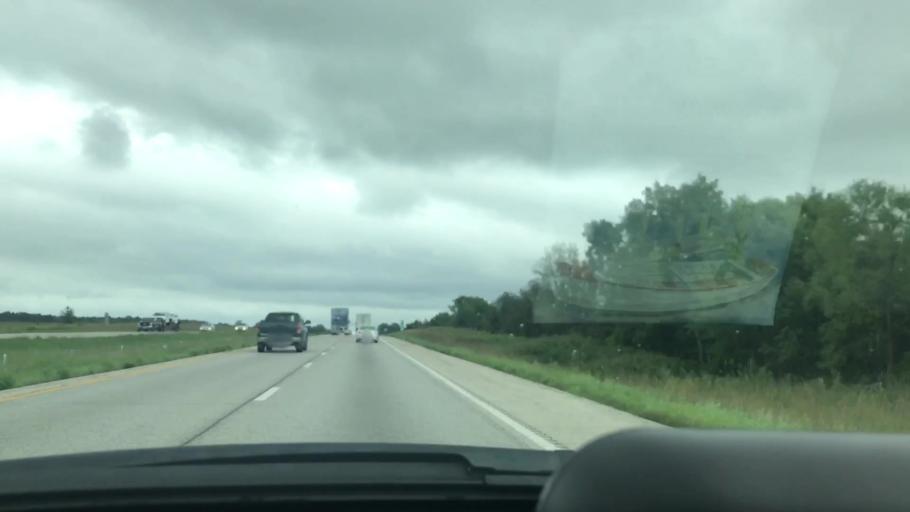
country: US
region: Missouri
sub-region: Greene County
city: Ash Grove
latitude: 37.1870
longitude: -93.6172
